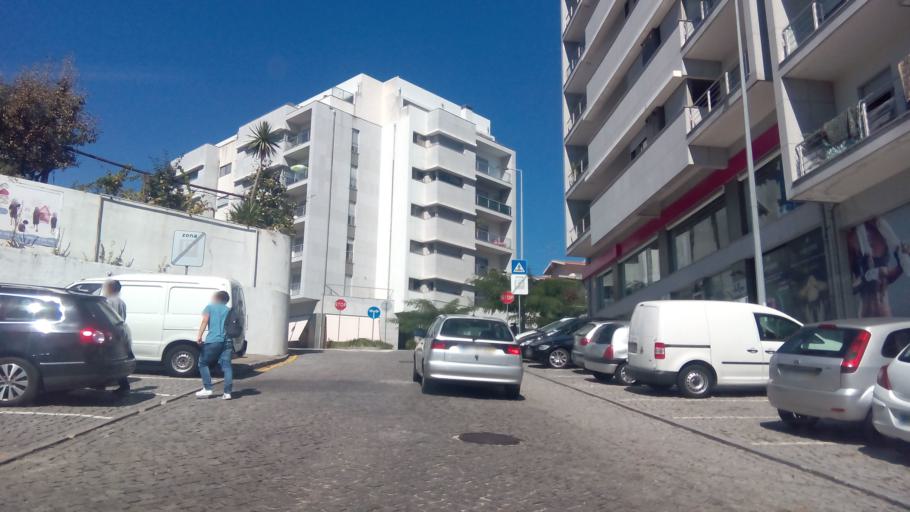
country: PT
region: Porto
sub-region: Paredes
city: Casteloes de Cepeda
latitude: 41.2066
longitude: -8.3356
